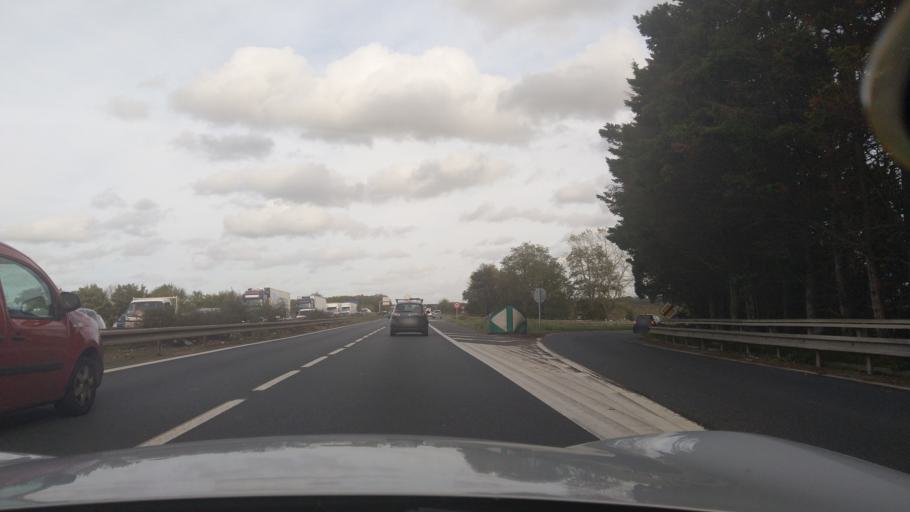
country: FR
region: Ile-de-France
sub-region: Departement du Val-d'Oise
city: Saint-Ouen-l'Aumone
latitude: 49.0506
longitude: 2.1476
